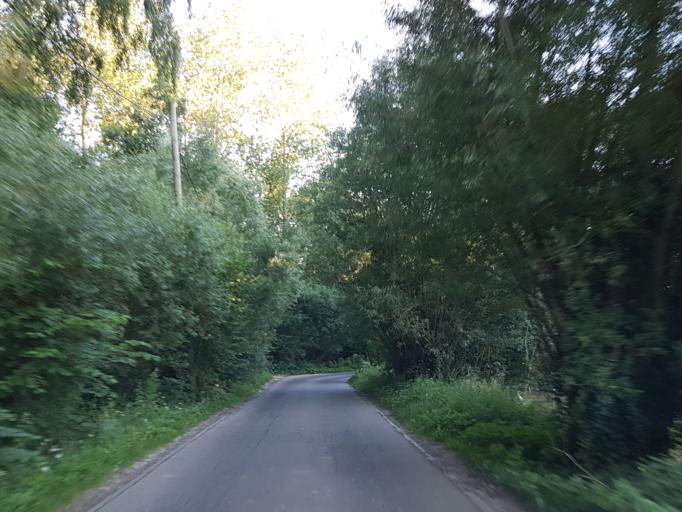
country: BE
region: Flanders
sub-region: Provincie Vlaams-Brabant
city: Dilbeek
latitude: 50.8709
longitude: 4.2291
